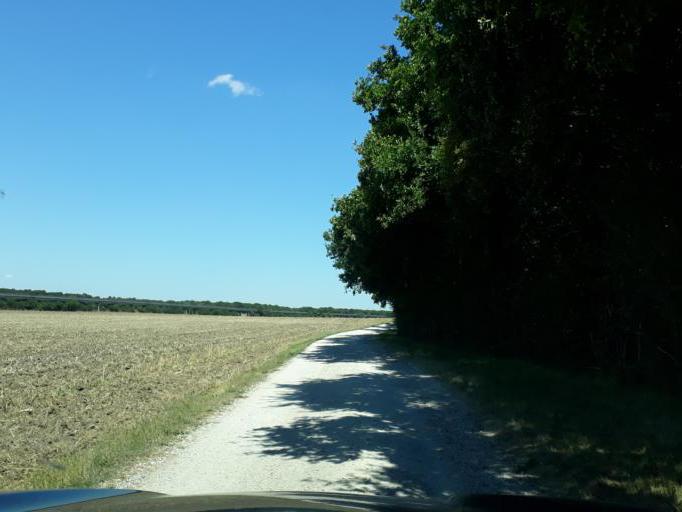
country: FR
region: Centre
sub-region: Departement du Loiret
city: Chevilly
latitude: 47.9907
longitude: 1.8871
